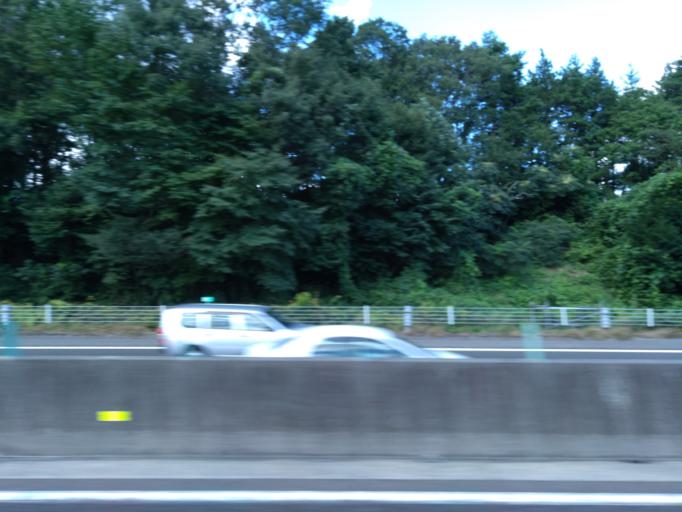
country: JP
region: Miyagi
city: Tomiya
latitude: 38.3355
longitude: 140.8555
